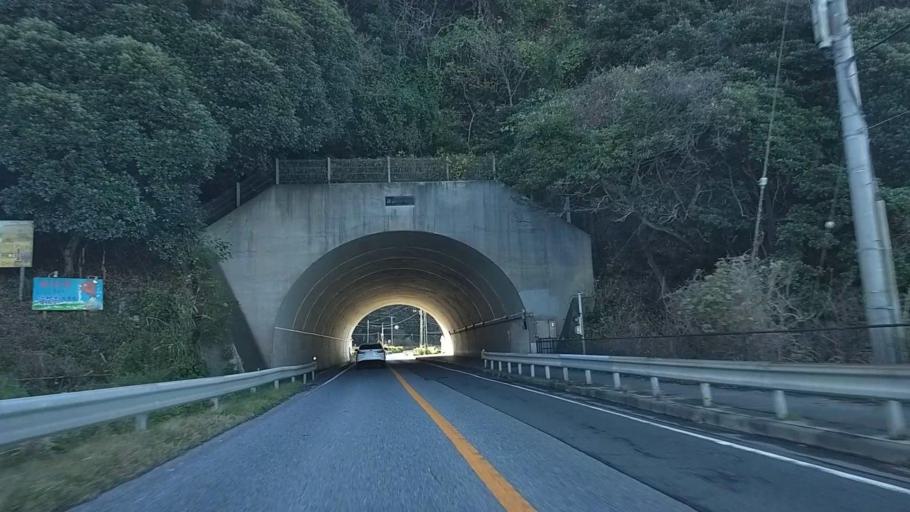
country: JP
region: Chiba
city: Futtsu
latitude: 35.1811
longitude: 139.8193
